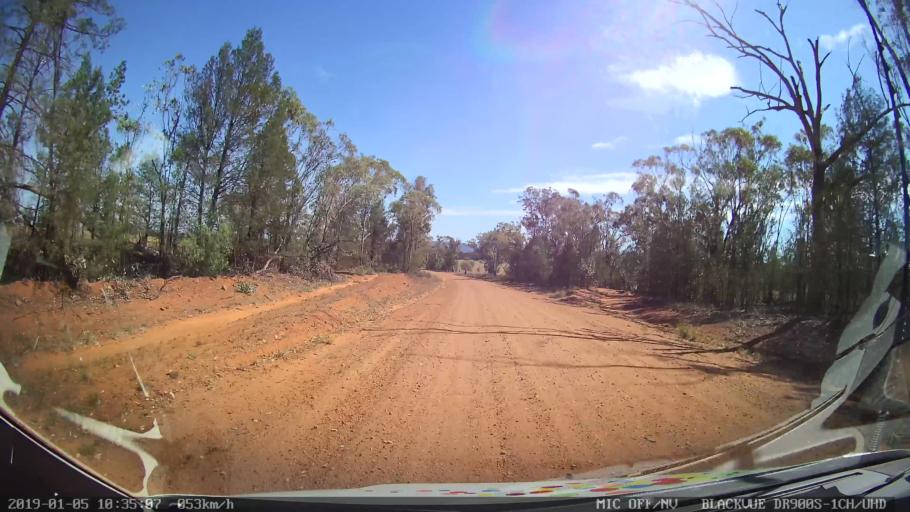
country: AU
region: New South Wales
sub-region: Gilgandra
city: Gilgandra
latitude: -31.4929
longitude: 148.9295
